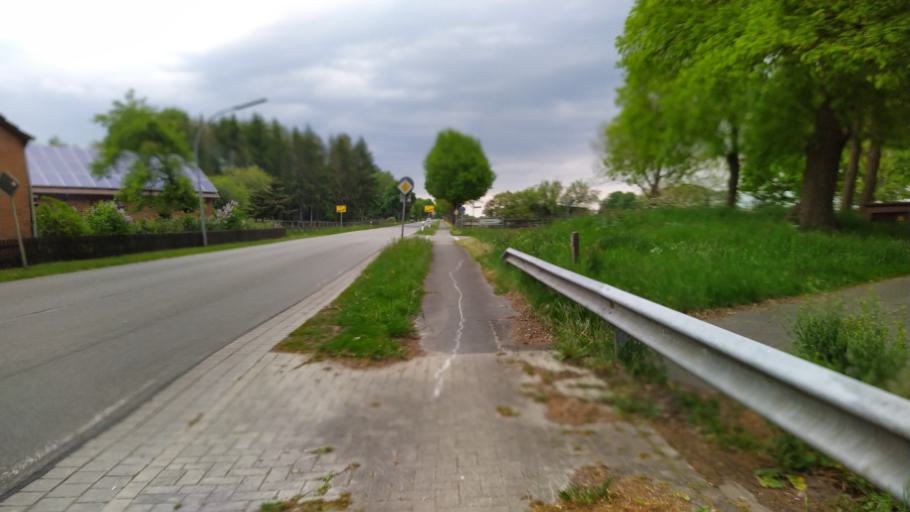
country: DE
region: Lower Saxony
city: Ostereistedt
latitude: 53.2743
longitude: 9.2041
